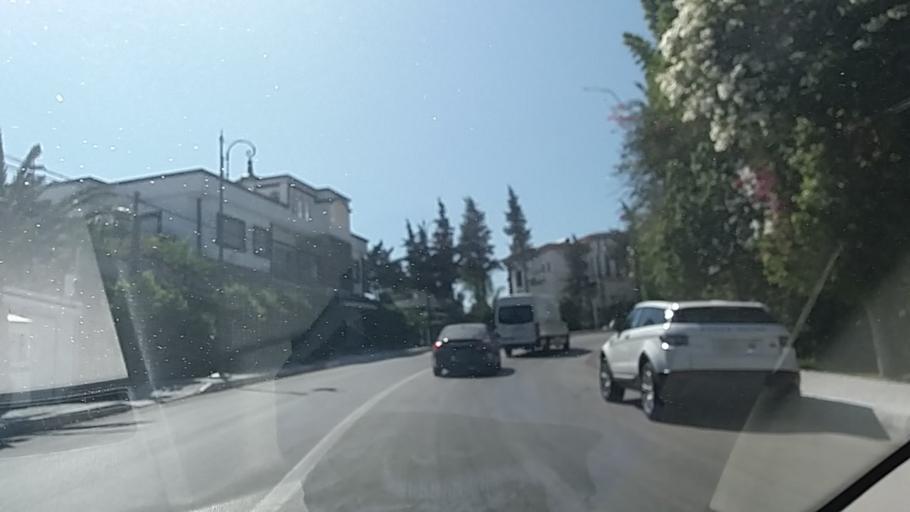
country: MA
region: Tanger-Tetouan
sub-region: Tanger-Assilah
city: Boukhalef
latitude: 35.7793
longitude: -5.8602
